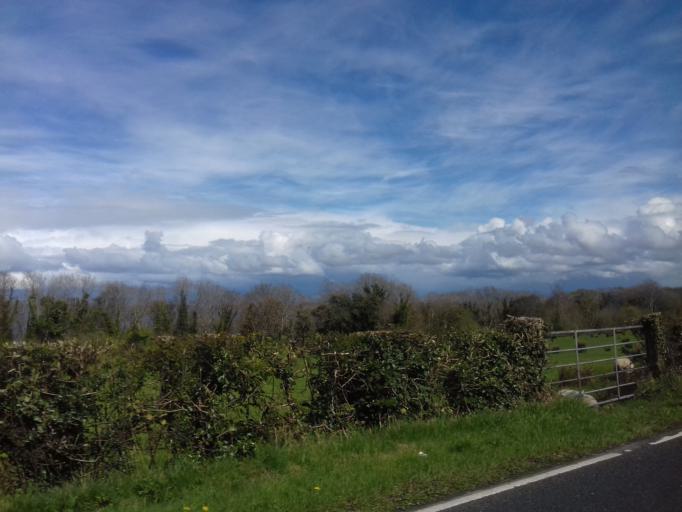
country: GB
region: Northern Ireland
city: Irvinestown
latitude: 54.4699
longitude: -7.8373
